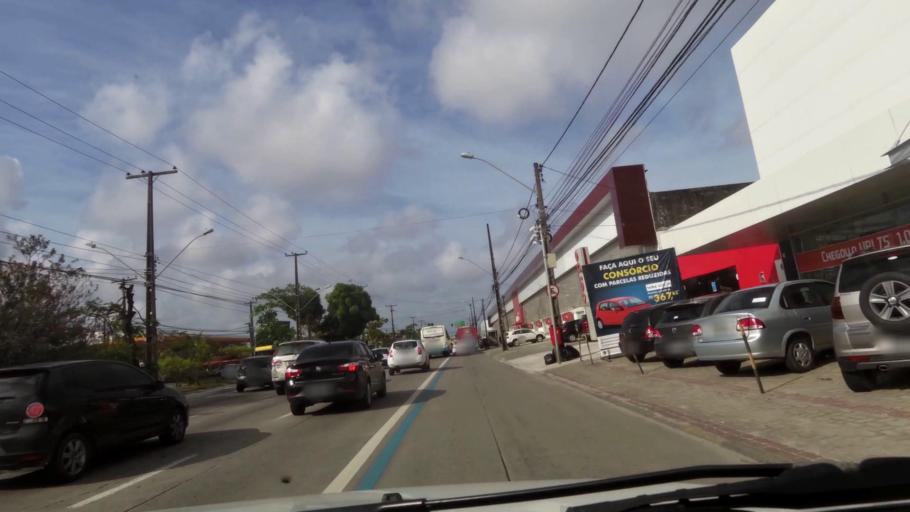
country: BR
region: Pernambuco
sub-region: Recife
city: Recife
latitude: -8.0902
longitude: -34.9082
